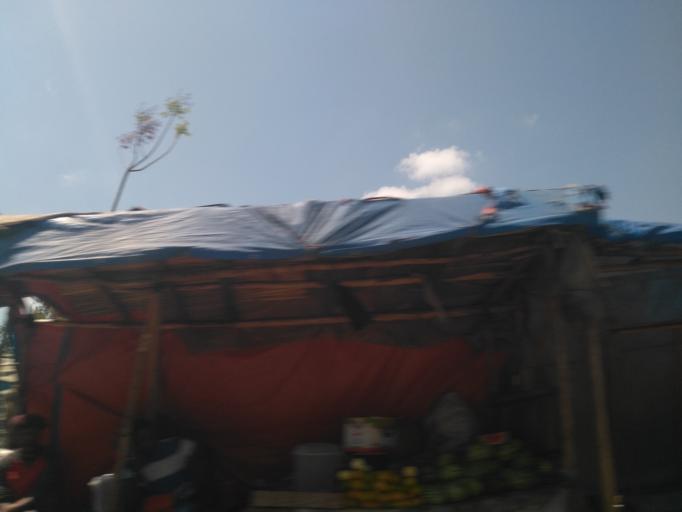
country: TZ
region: Arusha
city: Arusha
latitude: -3.3732
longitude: 36.6810
